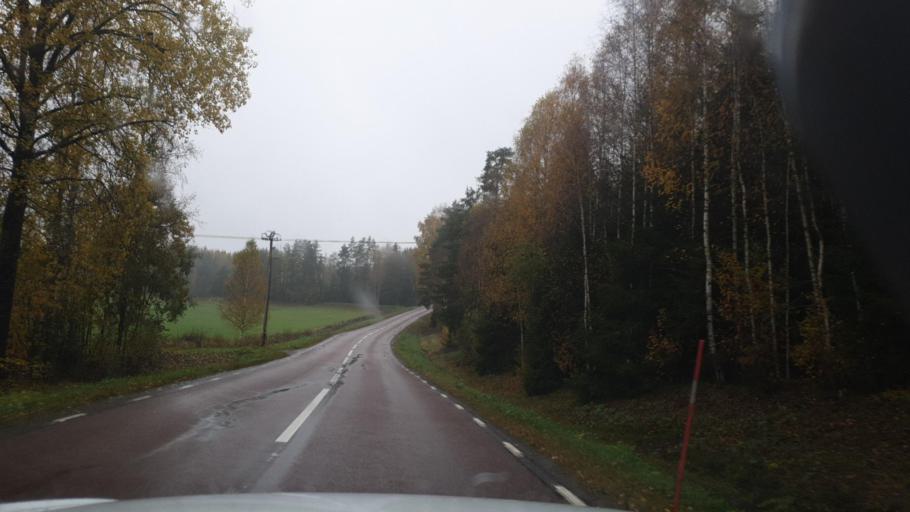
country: SE
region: Vaermland
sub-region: Eda Kommun
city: Amotfors
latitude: 59.7492
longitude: 12.2112
